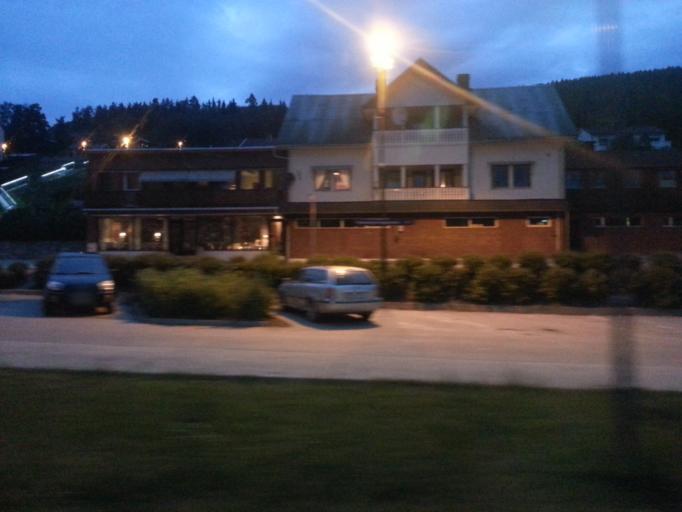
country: NO
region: Oppland
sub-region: Nord-Fron
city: Vinstra
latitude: 61.5947
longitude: 9.7486
